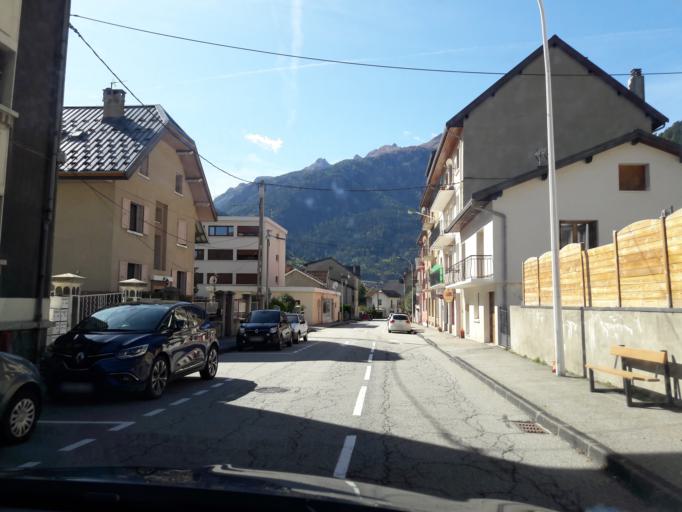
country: FR
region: Rhone-Alpes
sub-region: Departement de la Savoie
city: Modane
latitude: 45.2025
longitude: 6.6690
